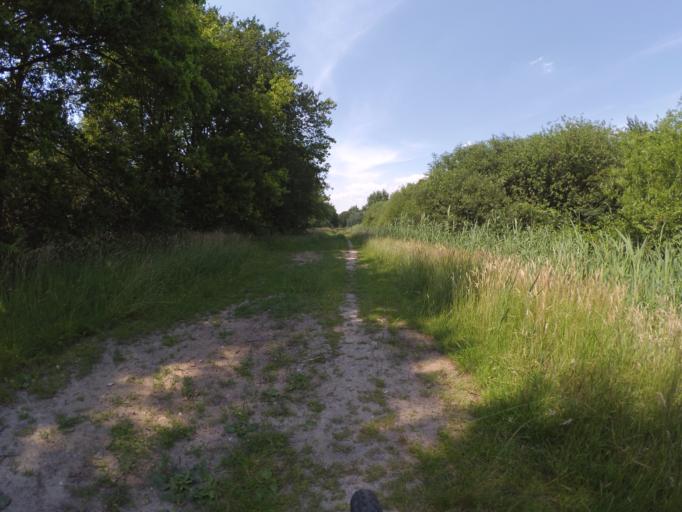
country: NL
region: Utrecht
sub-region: Gemeente Woudenberg
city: Woudenberg
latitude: 52.0941
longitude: 5.4380
